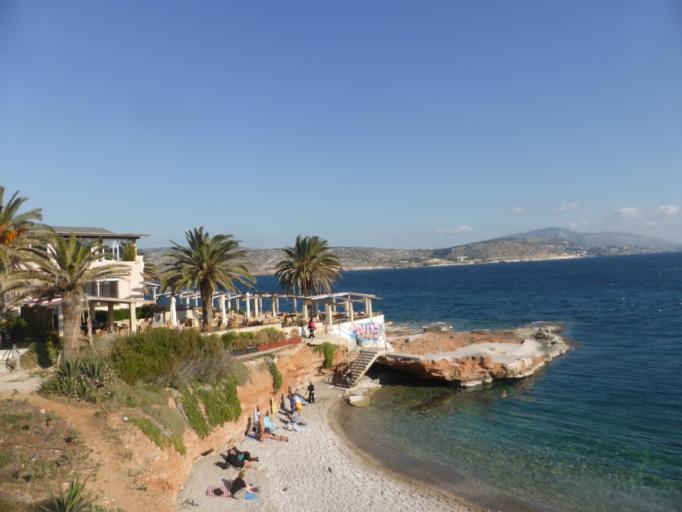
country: GR
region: Attica
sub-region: Nomarchia Anatolikis Attikis
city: Vari
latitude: 37.8123
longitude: 23.8006
